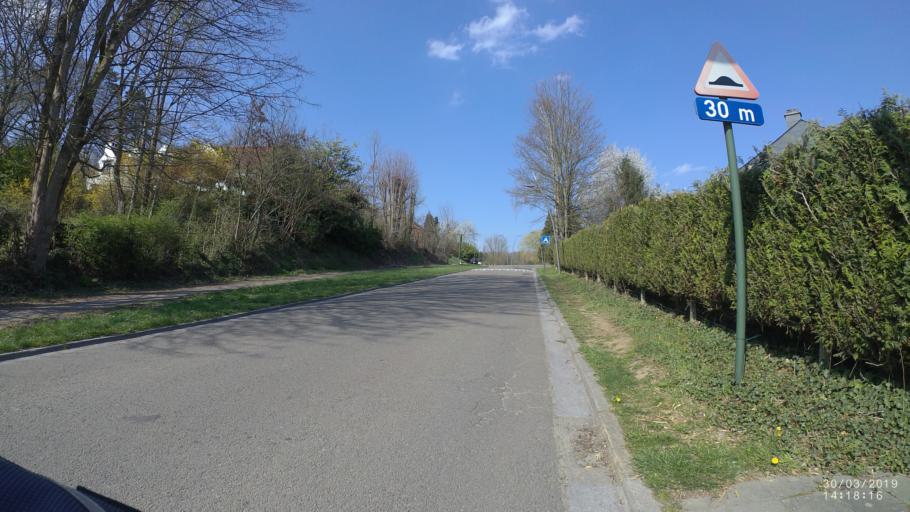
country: BE
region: Wallonia
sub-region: Province du Brabant Wallon
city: Wavre
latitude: 50.6987
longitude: 4.5774
